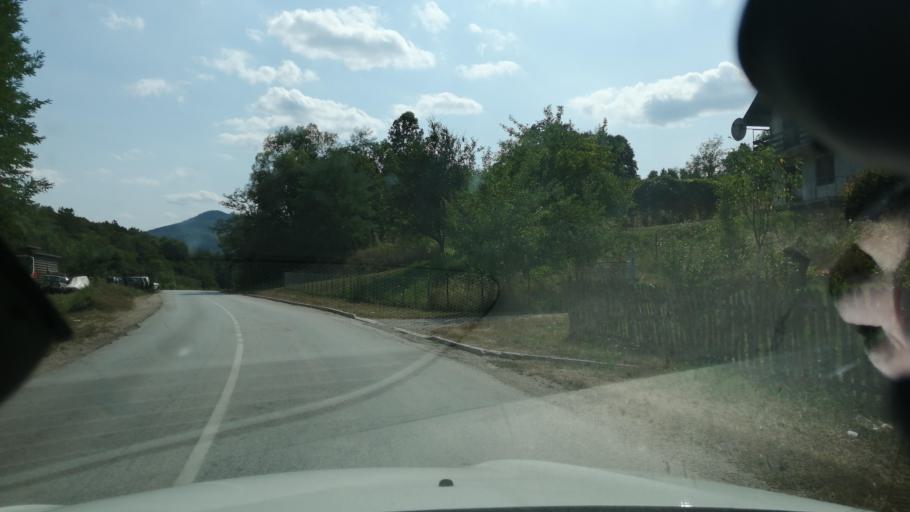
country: RS
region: Central Serbia
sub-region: Moravicki Okrug
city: Ivanjica
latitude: 43.6041
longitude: 20.2318
